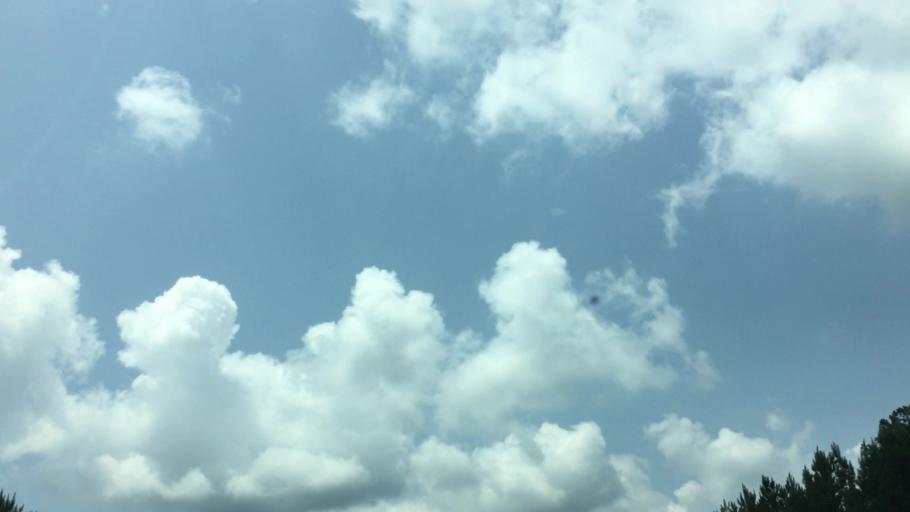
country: US
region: Georgia
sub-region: Fulton County
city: Chattahoochee Hills
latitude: 33.5673
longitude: -84.7051
